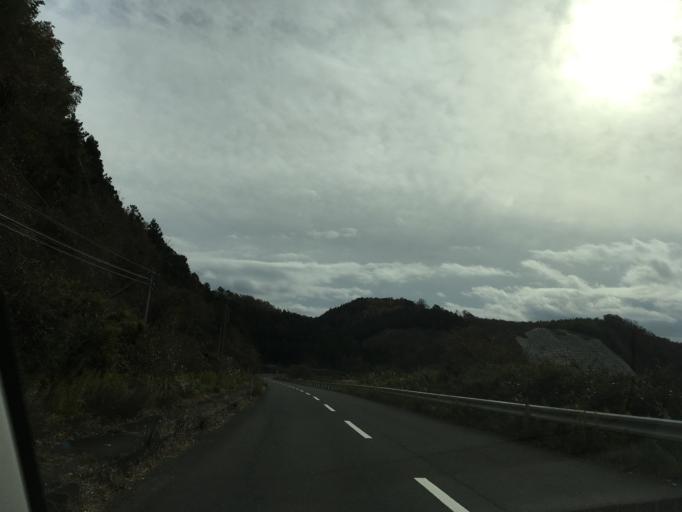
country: JP
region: Iwate
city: Ichinoseki
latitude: 38.7541
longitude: 141.2840
